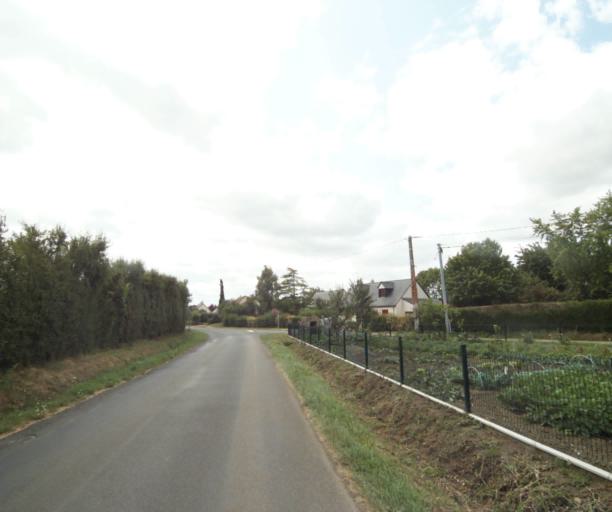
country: FR
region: Pays de la Loire
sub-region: Departement de la Sarthe
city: Sable-sur-Sarthe
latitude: 47.8568
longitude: -0.3549
